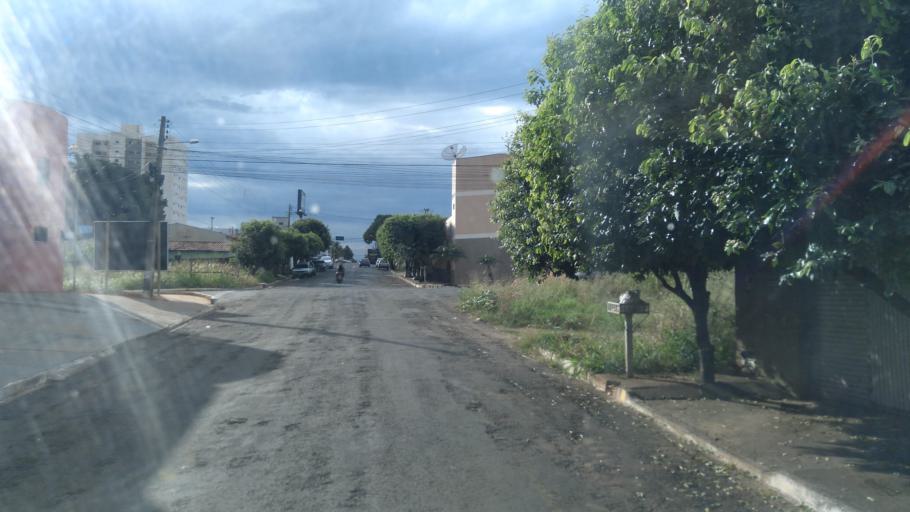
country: BR
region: Goias
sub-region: Mineiros
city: Mineiros
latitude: -17.5671
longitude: -52.5623
